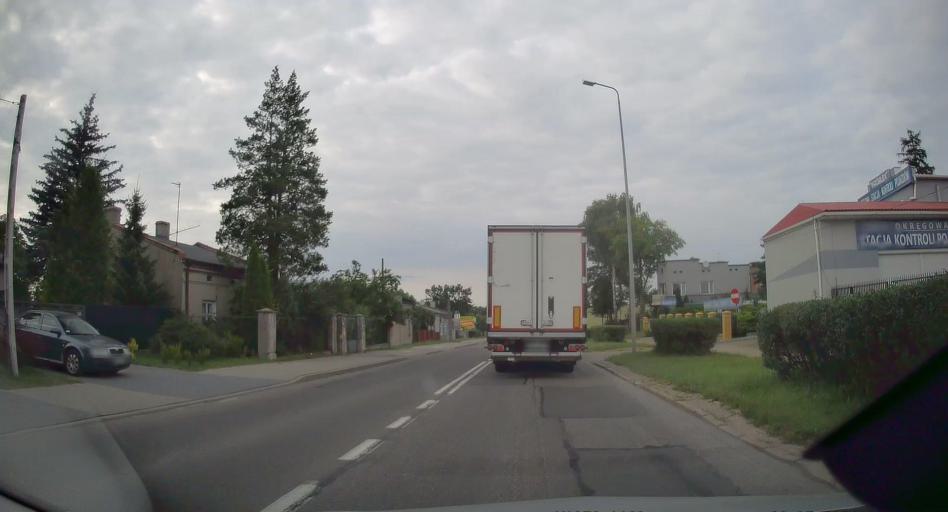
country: PL
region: Lodz Voivodeship
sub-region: Powiat radomszczanski
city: Radomsko
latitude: 51.0559
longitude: 19.4406
